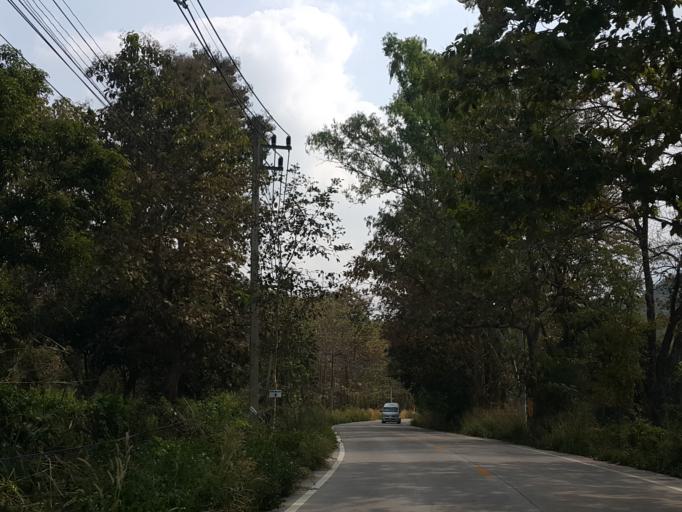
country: TH
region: Chiang Mai
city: Mae On
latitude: 18.8121
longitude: 99.2344
